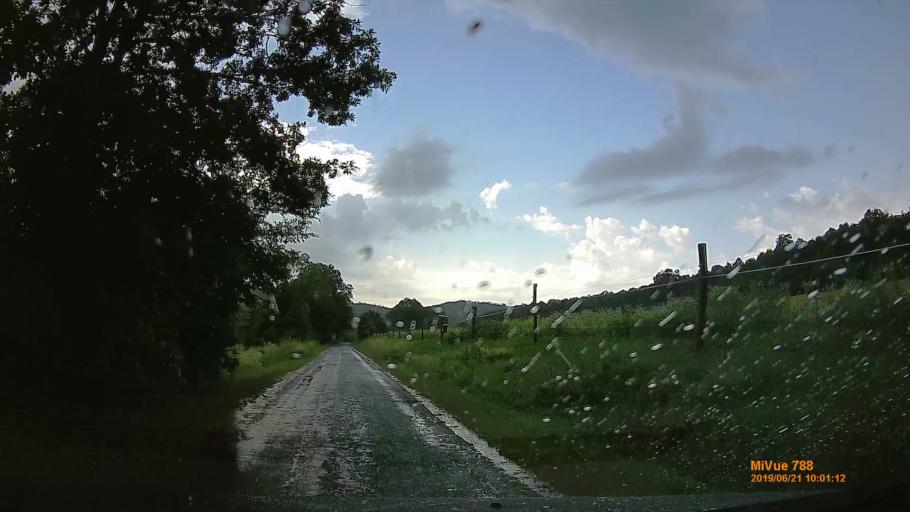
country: HU
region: Baranya
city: Buekkoesd
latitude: 46.2049
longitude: 17.9734
